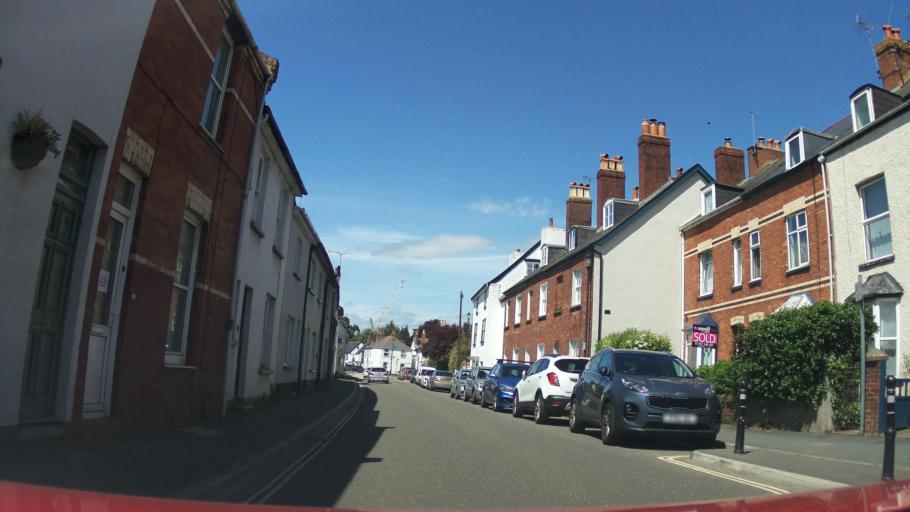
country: GB
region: England
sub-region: Devon
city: Topsham
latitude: 50.6863
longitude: -3.4673
